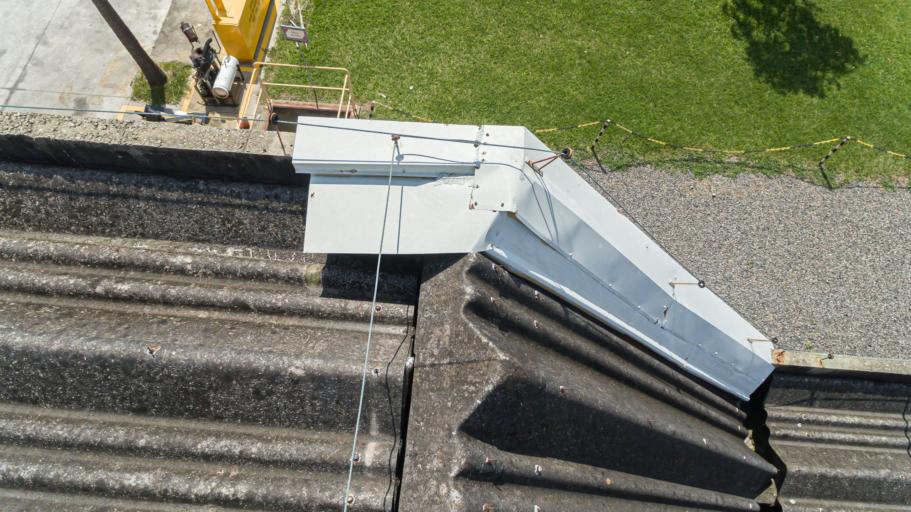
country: BR
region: Sao Paulo
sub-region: Cacapava
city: Cacapava
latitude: -23.1319
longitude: -45.7535
